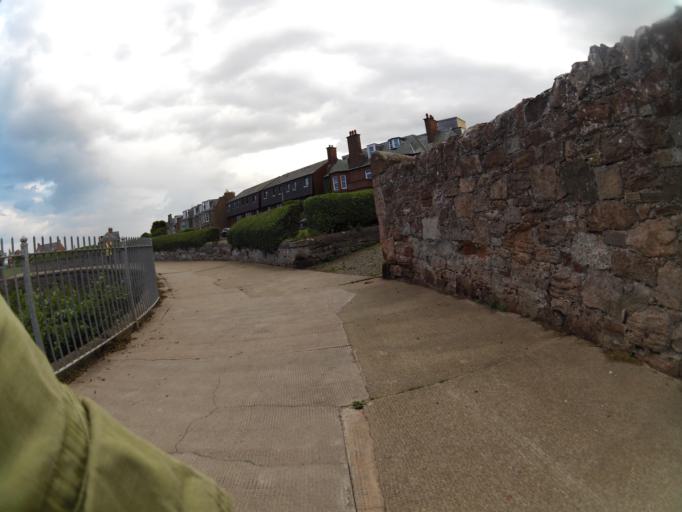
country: GB
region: Scotland
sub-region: East Lothian
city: Dunbar
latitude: 56.0058
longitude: -2.5258
